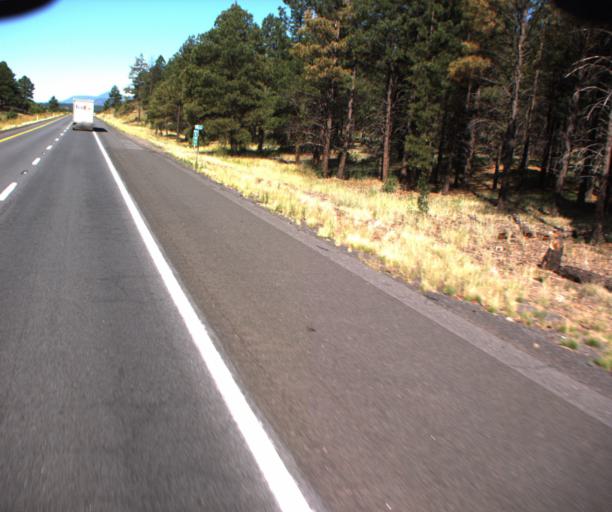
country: US
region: Arizona
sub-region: Coconino County
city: Parks
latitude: 35.2509
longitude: -111.9596
